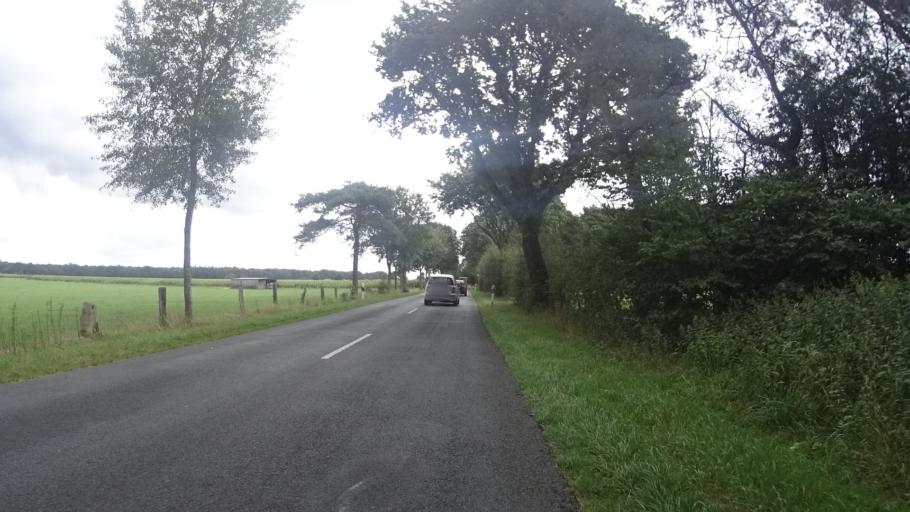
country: DE
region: Lower Saxony
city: Elmlohe
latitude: 53.5788
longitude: 8.7708
